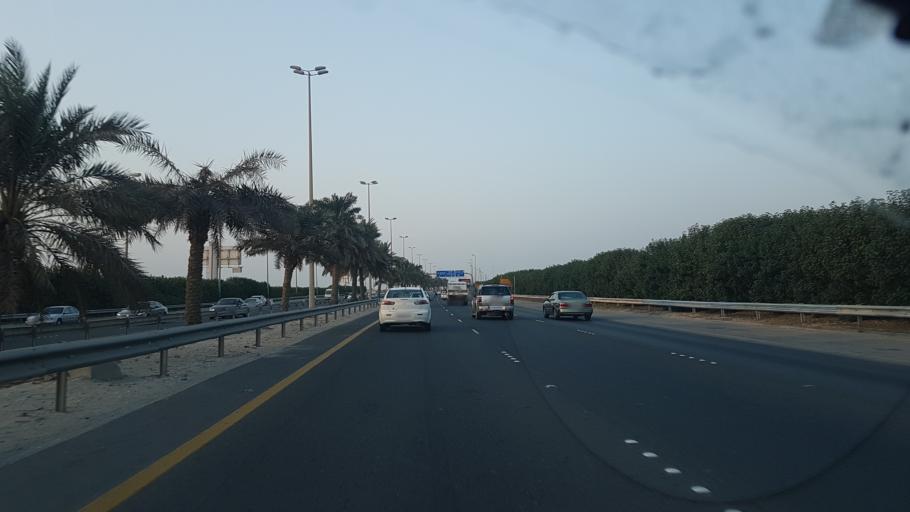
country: BH
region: Northern
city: Madinat `Isa
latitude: 26.1728
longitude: 50.5025
